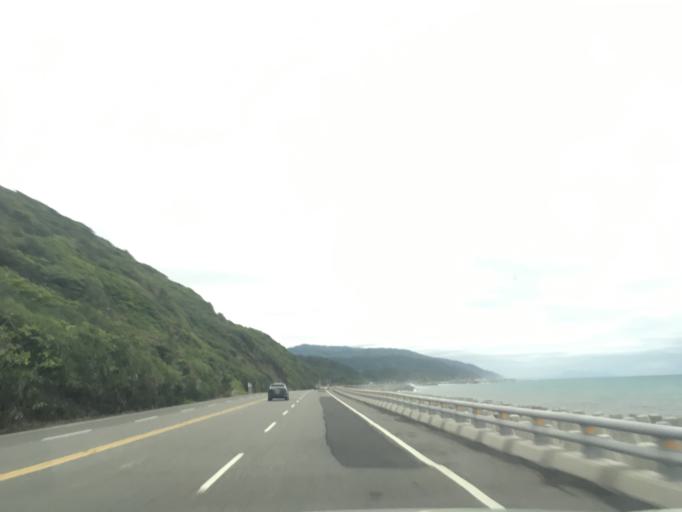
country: TW
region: Taiwan
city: Hengchun
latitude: 22.3171
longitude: 120.8915
